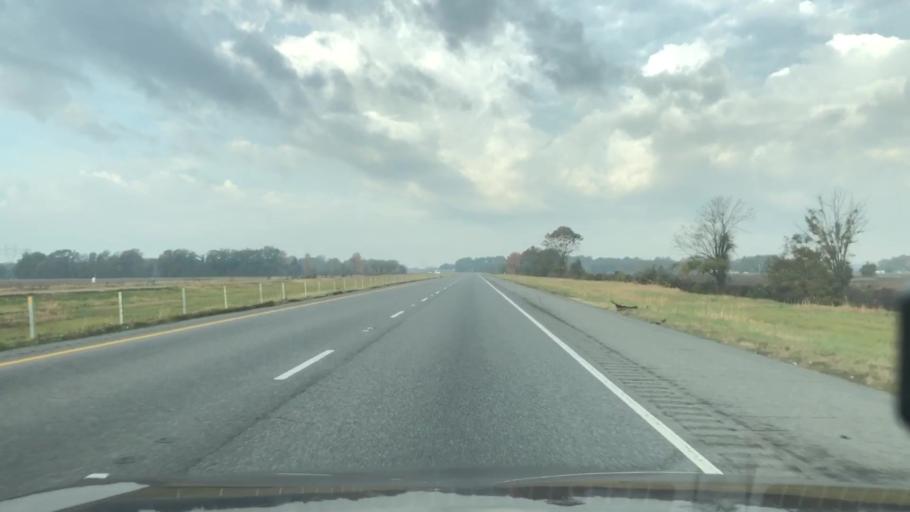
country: US
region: Louisiana
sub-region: Madison Parish
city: Tallulah
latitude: 32.4171
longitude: -91.2846
